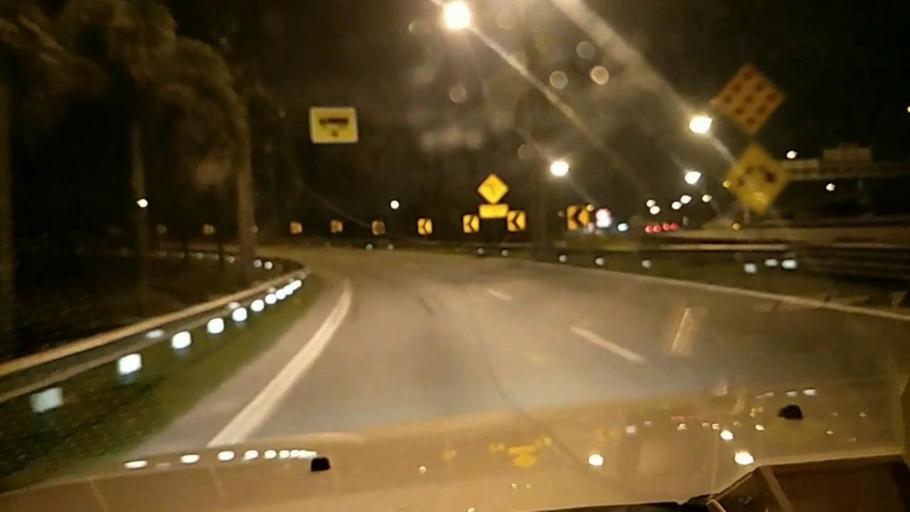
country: MY
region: Selangor
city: Shah Alam
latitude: 3.0932
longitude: 101.5504
